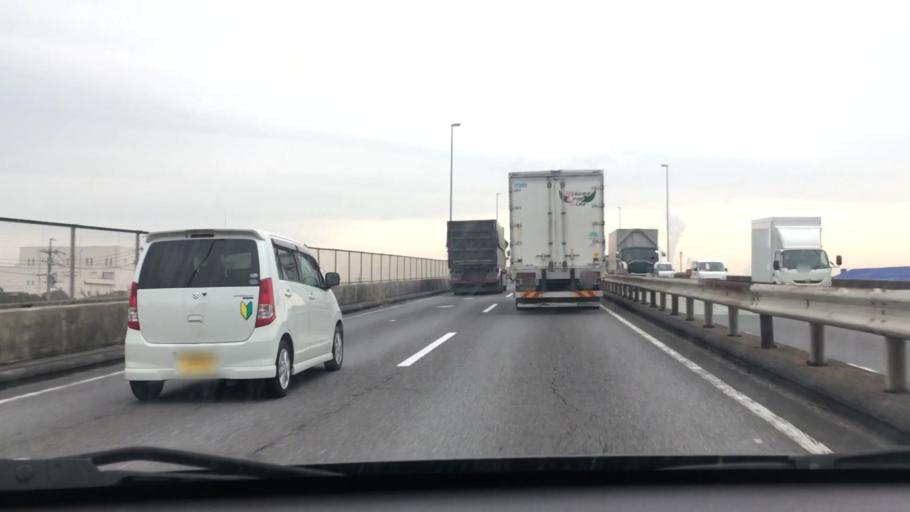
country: JP
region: Mie
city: Yokkaichi
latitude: 34.9468
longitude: 136.6203
